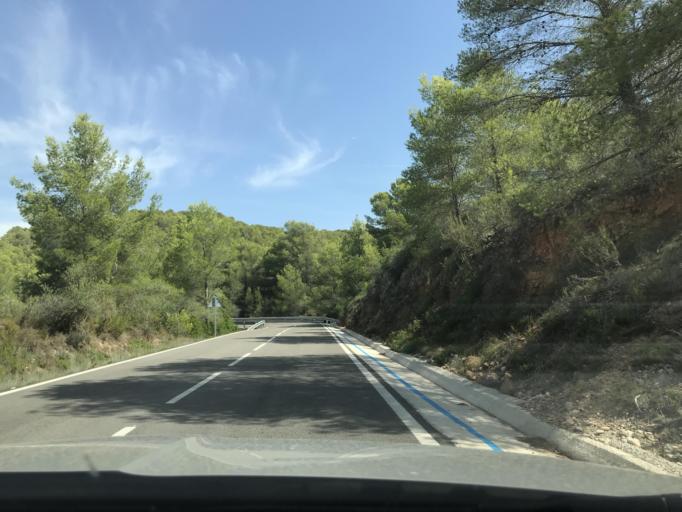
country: ES
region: Catalonia
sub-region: Provincia de Tarragona
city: Salomo
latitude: 41.1923
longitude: 1.3846
